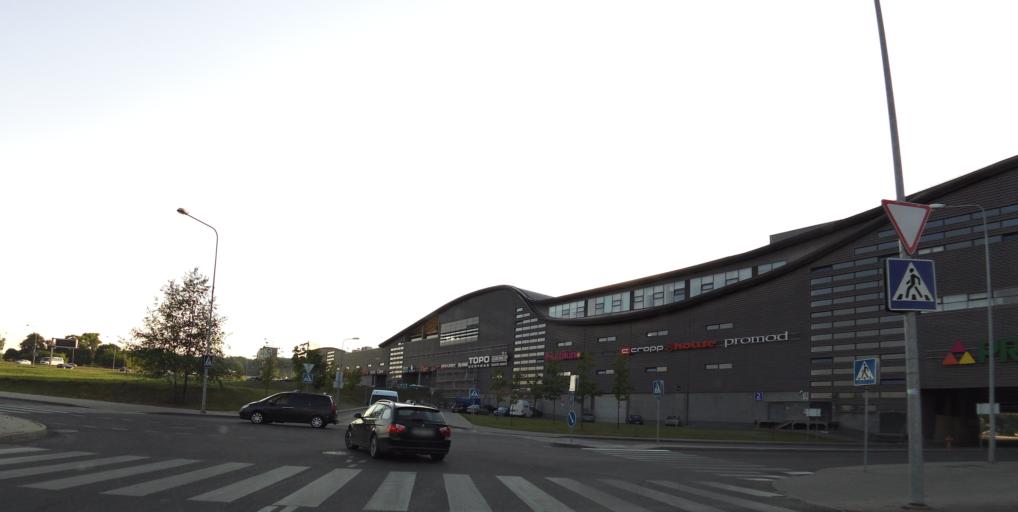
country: LT
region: Vilnius County
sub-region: Vilnius
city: Vilnius
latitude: 54.7141
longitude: 25.2767
